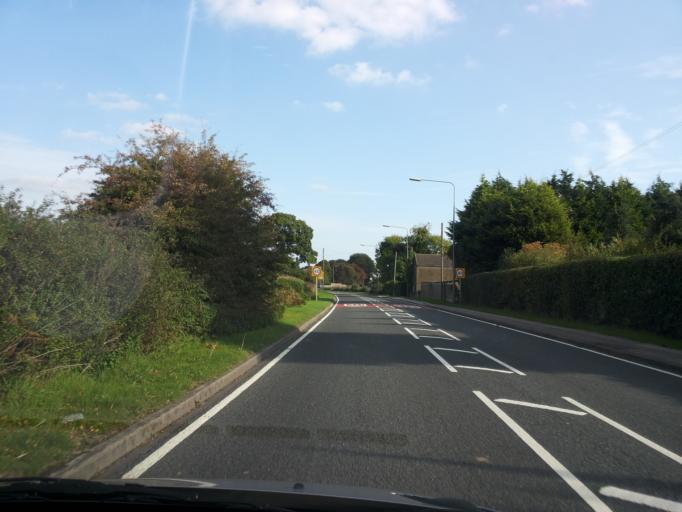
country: GB
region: England
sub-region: North Yorkshire
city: Camblesforth
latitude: 53.7279
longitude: -1.0297
